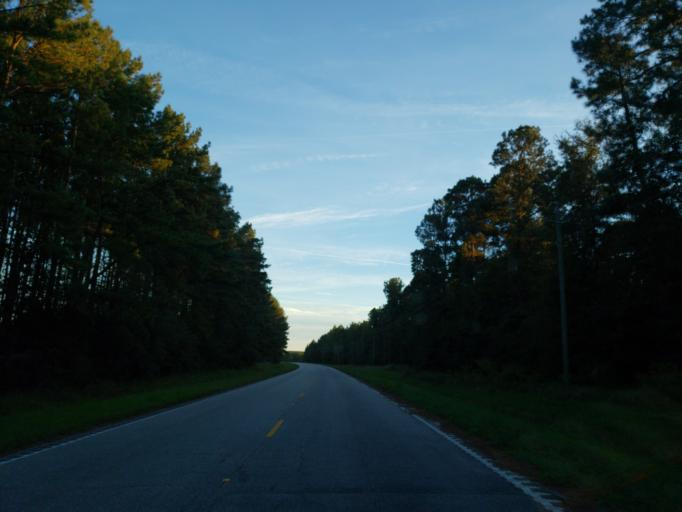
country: US
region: Mississippi
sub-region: Wayne County
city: Belmont
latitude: 31.4132
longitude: -88.4712
